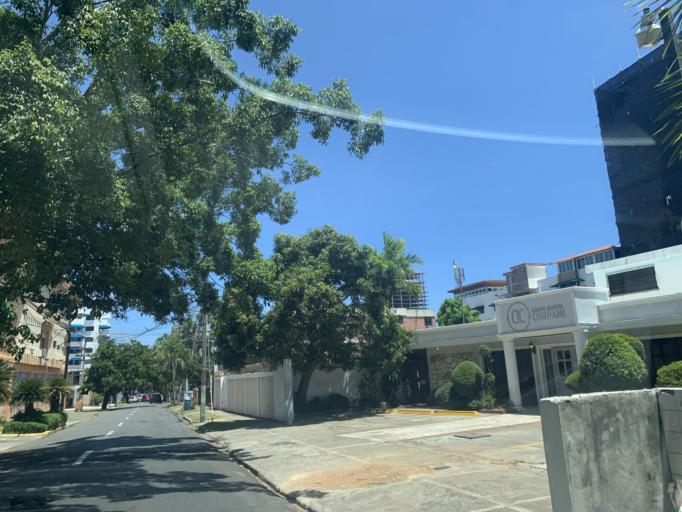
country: DO
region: Nacional
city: Ciudad Nueva
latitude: 18.4640
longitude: -69.9056
